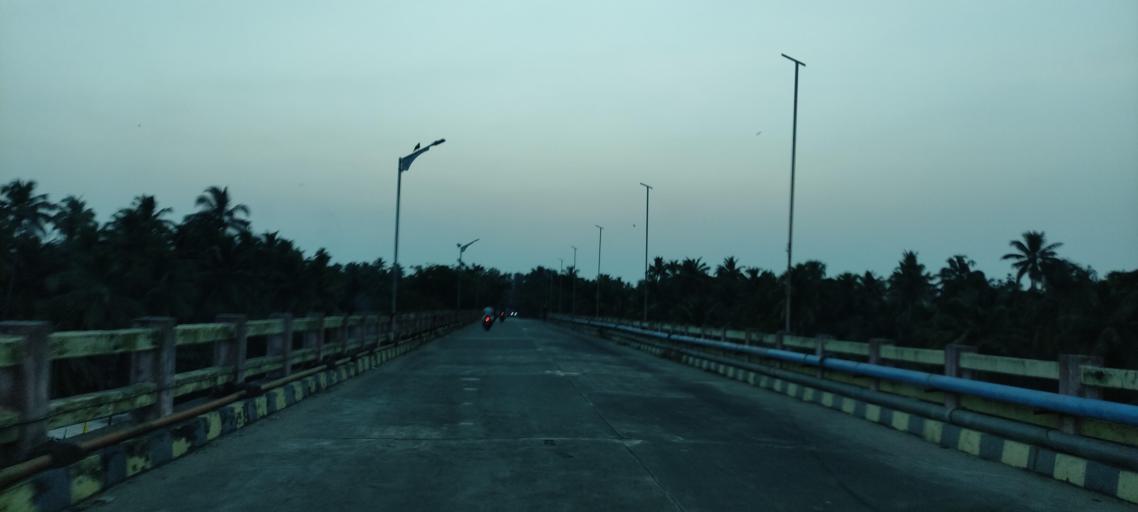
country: IN
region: Kerala
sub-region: Alappuzha
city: Kayankulam
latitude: 9.1153
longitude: 76.4766
